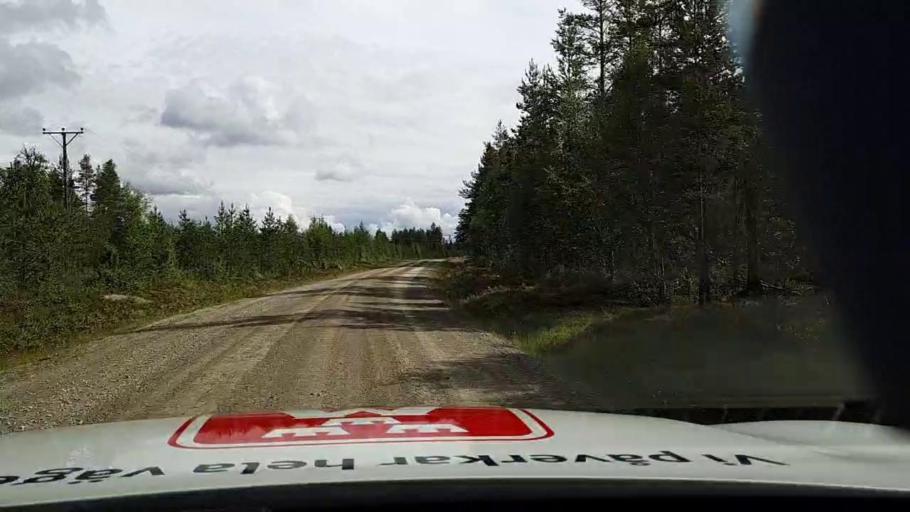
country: SE
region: Jaemtland
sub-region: Are Kommun
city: Jarpen
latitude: 62.5045
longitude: 13.4996
